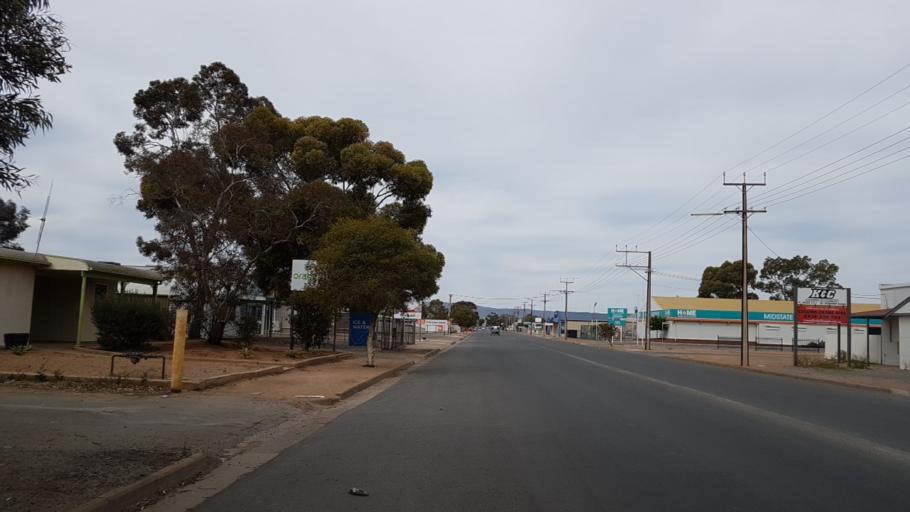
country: AU
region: South Australia
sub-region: Port Pirie City and Dists
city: Port Pirie
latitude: -33.1933
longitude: 138.0057
